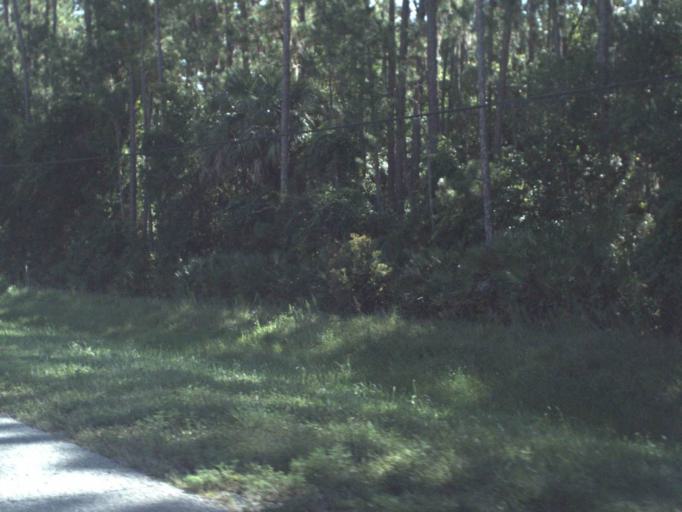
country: US
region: Florida
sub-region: Alachua County
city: Hawthorne
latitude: 29.5254
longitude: -82.1025
